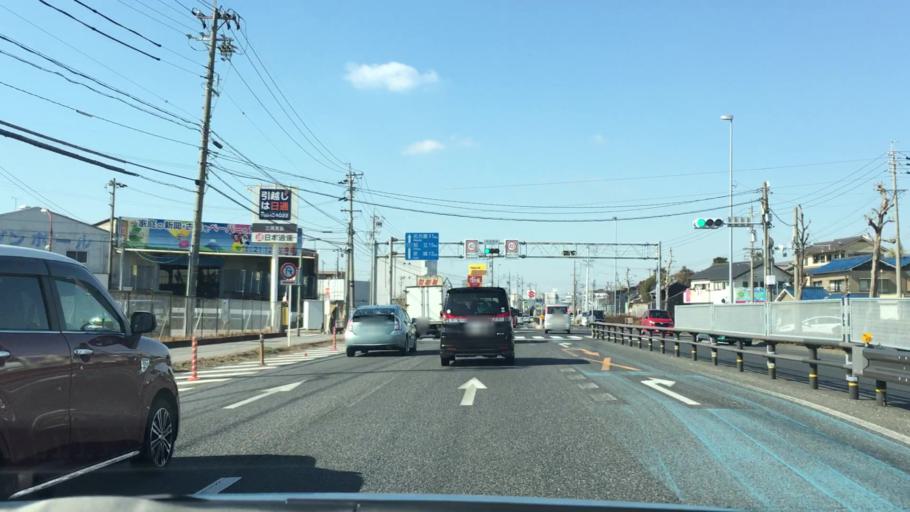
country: JP
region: Aichi
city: Okazaki
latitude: 34.9481
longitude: 137.1851
